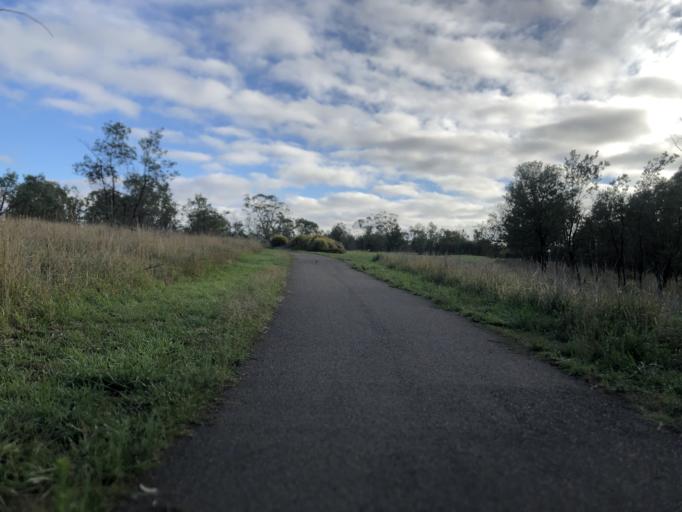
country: AU
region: New South Wales
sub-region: Orange Municipality
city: Orange
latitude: -33.3274
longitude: 149.0868
